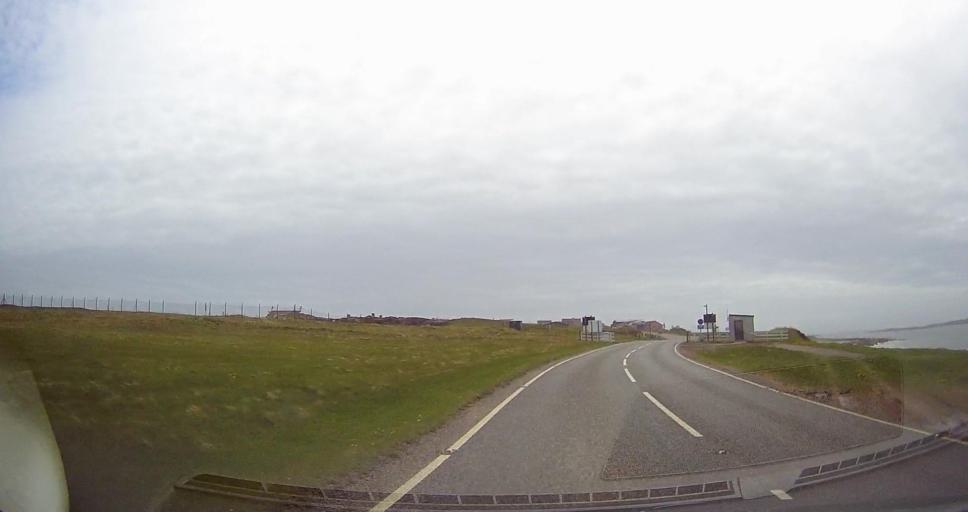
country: GB
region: Scotland
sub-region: Shetland Islands
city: Sandwick
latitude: 59.8805
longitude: -1.3055
